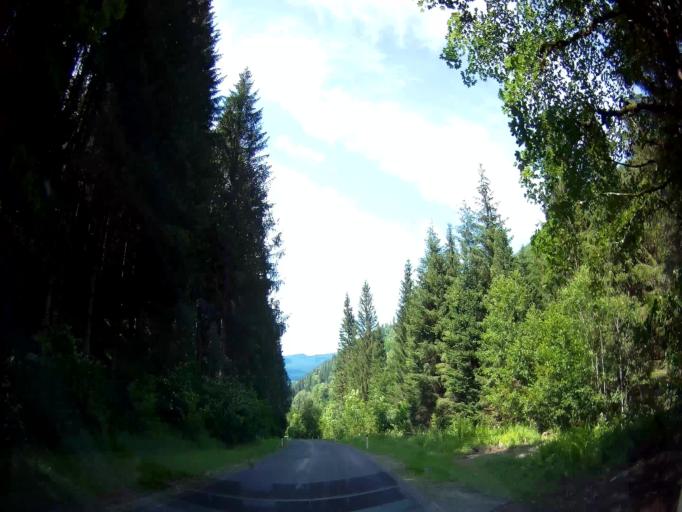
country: AT
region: Styria
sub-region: Politischer Bezirk Murau
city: Stadl an der Mur
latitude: 47.0513
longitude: 13.9970
